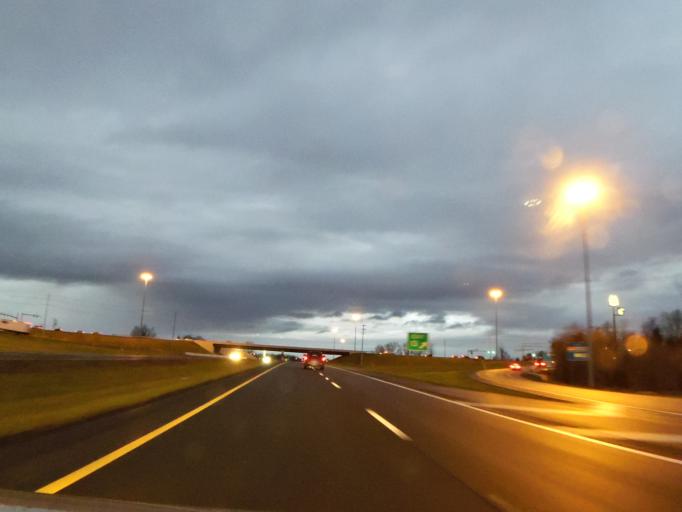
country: US
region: Tennessee
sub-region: Washington County
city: Gray
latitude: 36.4055
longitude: -82.4746
